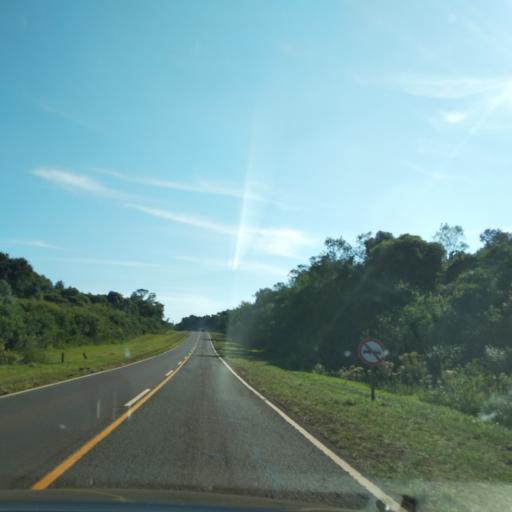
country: AR
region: Misiones
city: Santo Pipo
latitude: -27.1144
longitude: -55.3590
